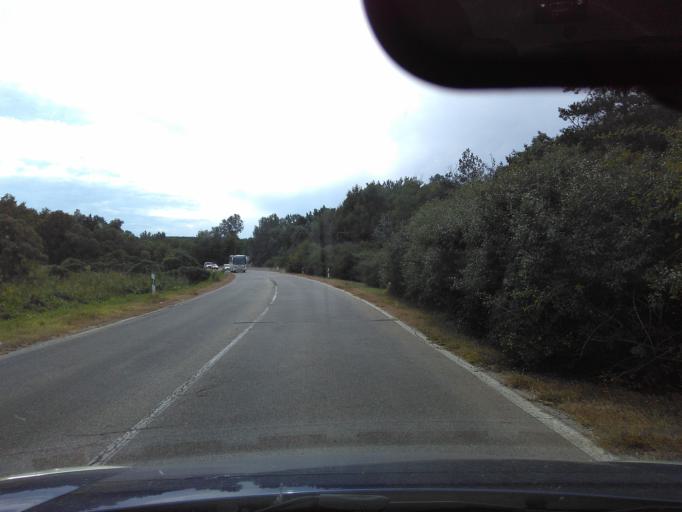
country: HU
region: Pest
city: Domony
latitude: 47.6256
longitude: 19.4145
